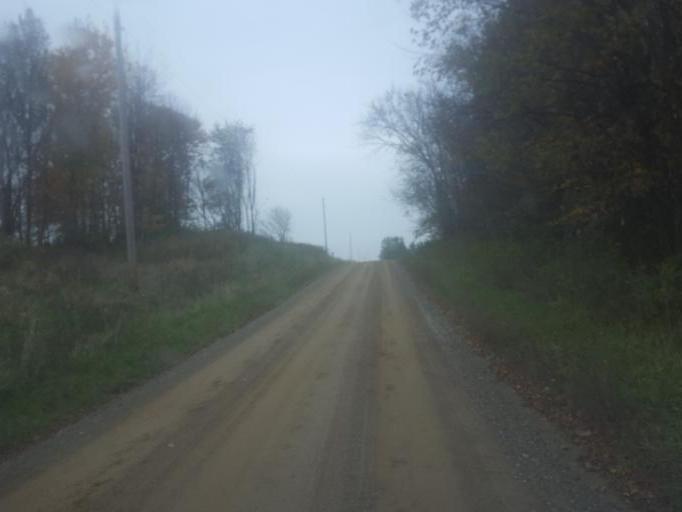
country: US
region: Ohio
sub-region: Wayne County
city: Shreve
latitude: 40.6452
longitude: -82.1012
